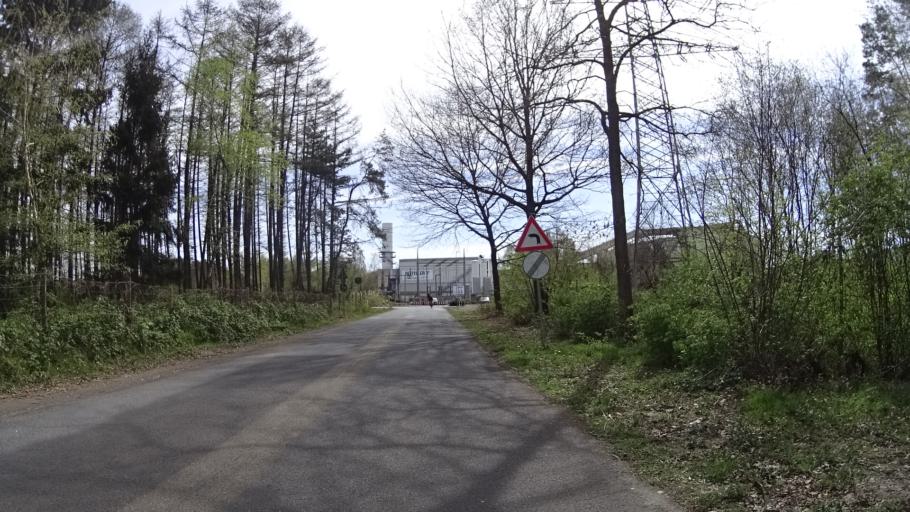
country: DE
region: Lower Saxony
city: Lingen
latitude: 52.4704
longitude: 7.3162
